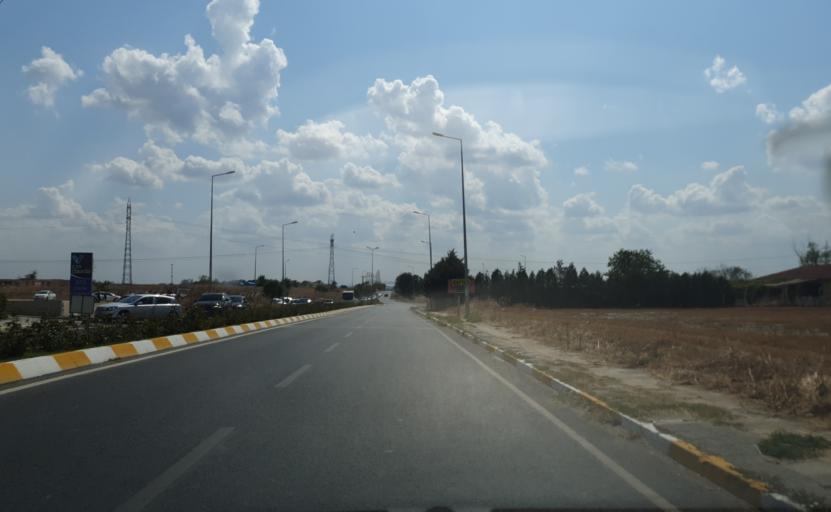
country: TR
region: Kirklareli
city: Luleburgaz
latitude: 41.3853
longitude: 27.3466
